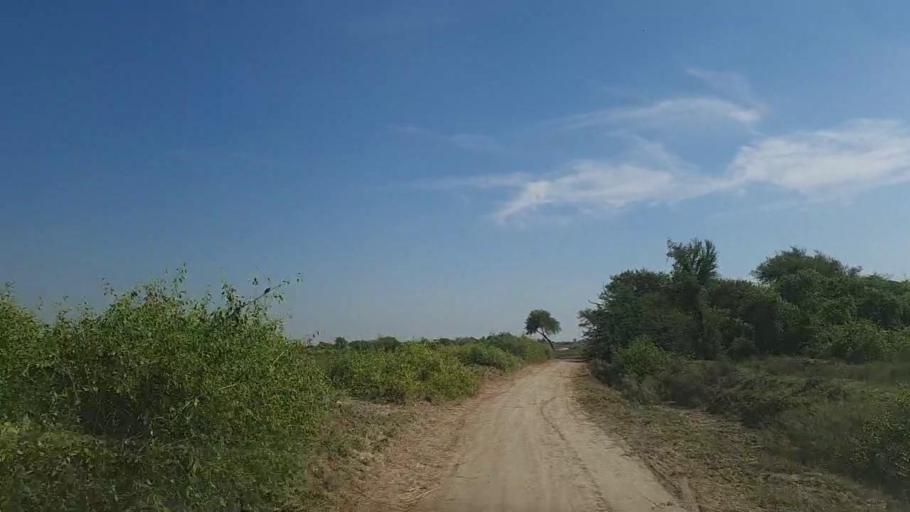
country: PK
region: Sindh
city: Mirpur Batoro
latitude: 24.7563
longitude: 68.3013
